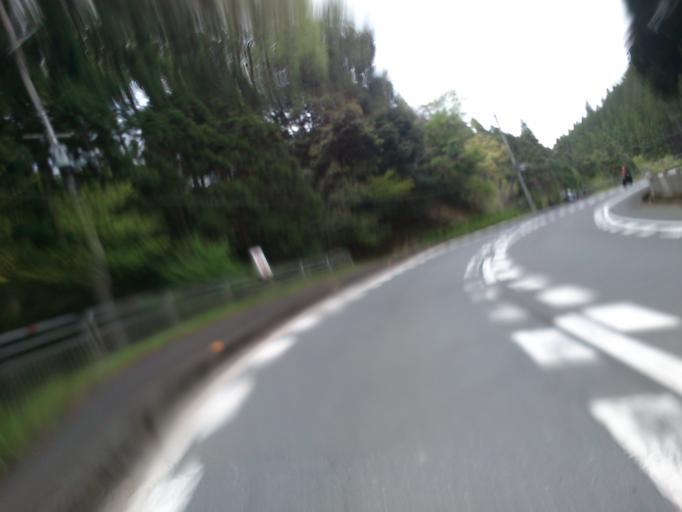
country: JP
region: Kyoto
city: Kameoka
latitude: 35.1578
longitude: 135.5140
